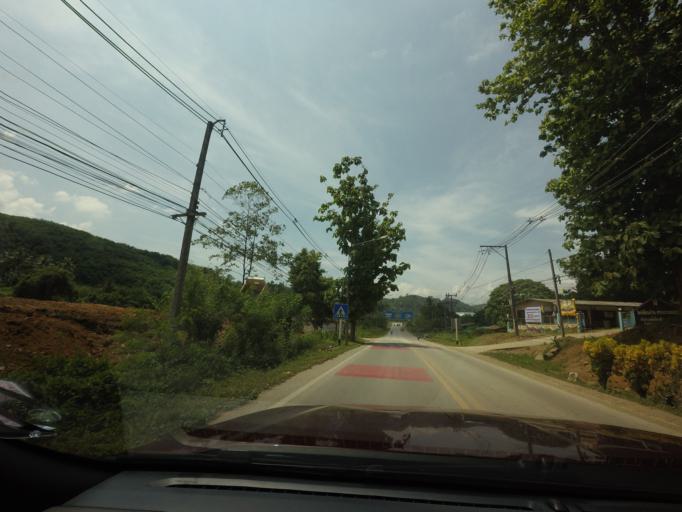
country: TH
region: Yala
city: Betong
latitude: 5.8164
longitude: 101.0904
